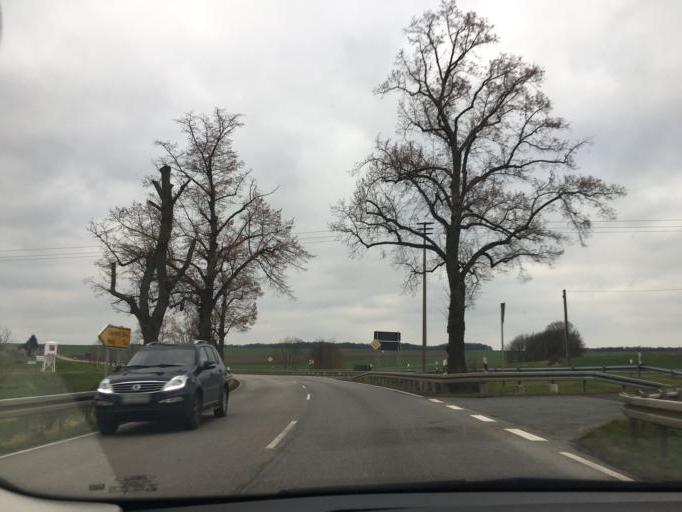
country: DE
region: Thuringia
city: Juckelberg
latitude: 50.9656
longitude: 12.6543
